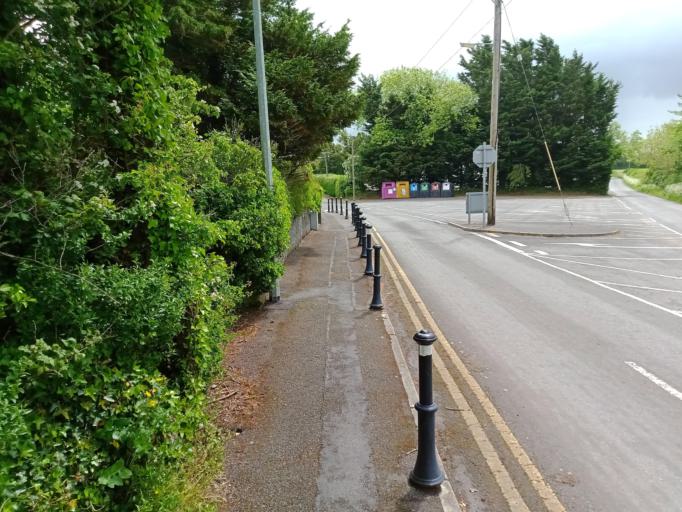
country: IE
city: Ballylinan
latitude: 52.9666
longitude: -7.0791
